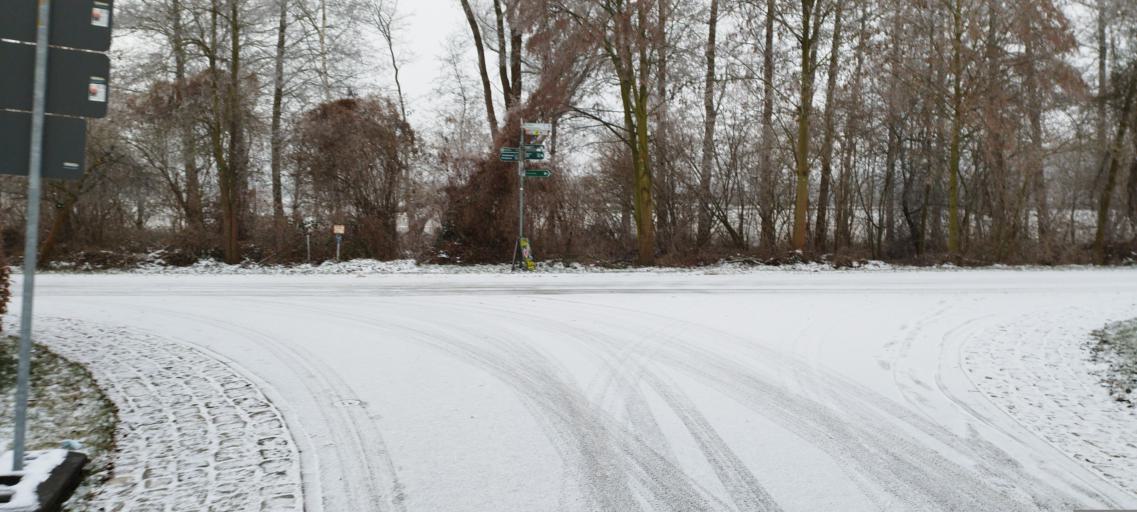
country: DE
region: Brandenburg
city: Schlepzig
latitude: 52.0235
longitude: 13.8887
